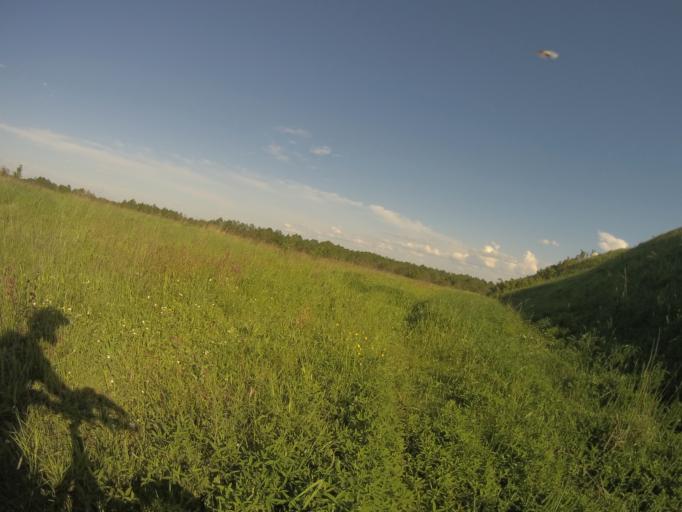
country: RU
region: Vladimir
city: Orgtrud
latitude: 56.1952
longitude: 40.7837
